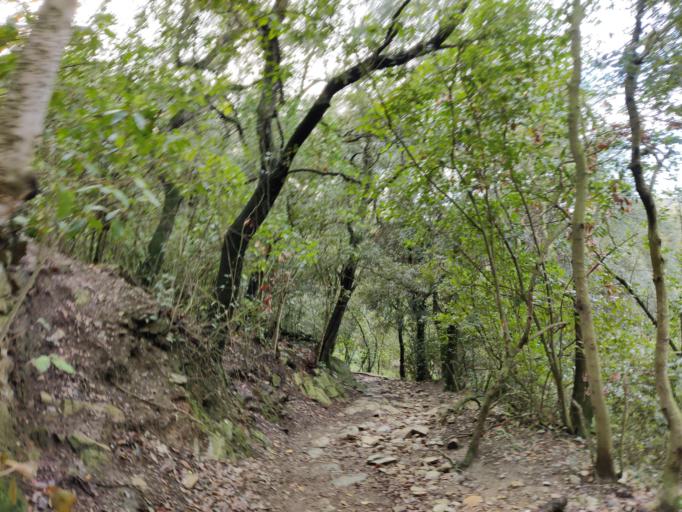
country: ES
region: Catalonia
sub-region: Provincia de Barcelona
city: Sarria-Sant Gervasi
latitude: 41.4198
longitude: 2.1128
